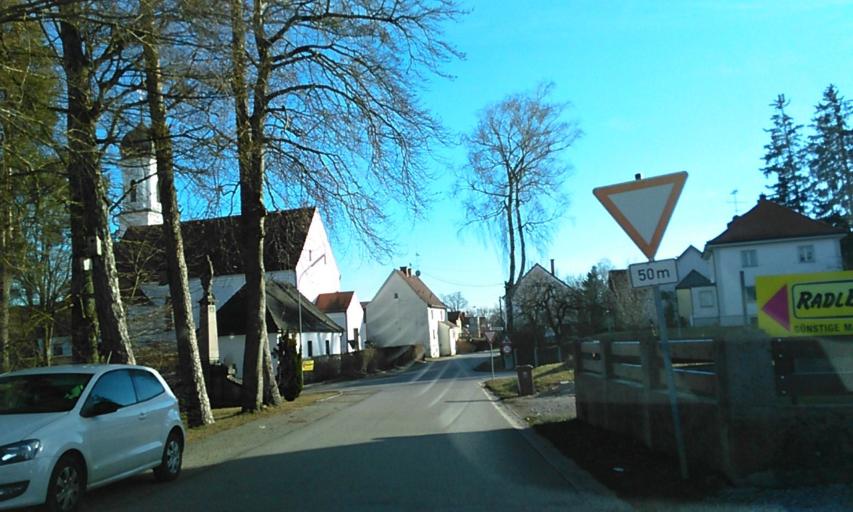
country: DE
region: Bavaria
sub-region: Swabia
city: Steindorf
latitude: 48.2174
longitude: 11.0014
